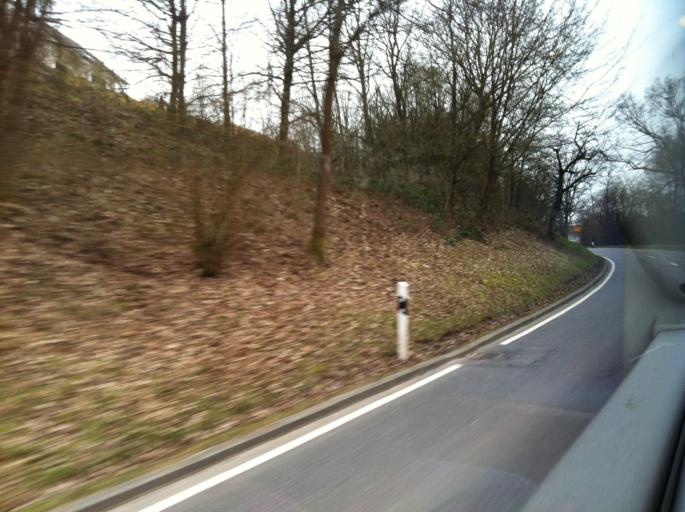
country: DE
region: Baden-Wuerttemberg
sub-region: Karlsruhe Region
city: Fahrenbach
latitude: 49.3984
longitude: 9.1449
